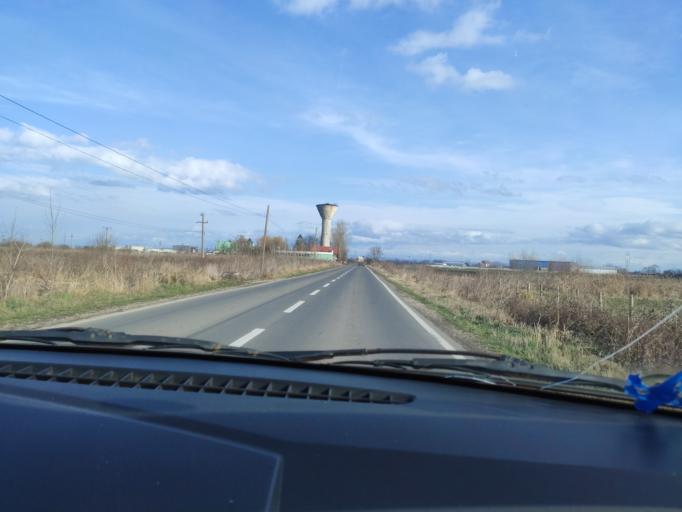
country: RO
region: Brasov
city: Codlea
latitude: 45.7128
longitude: 25.4655
